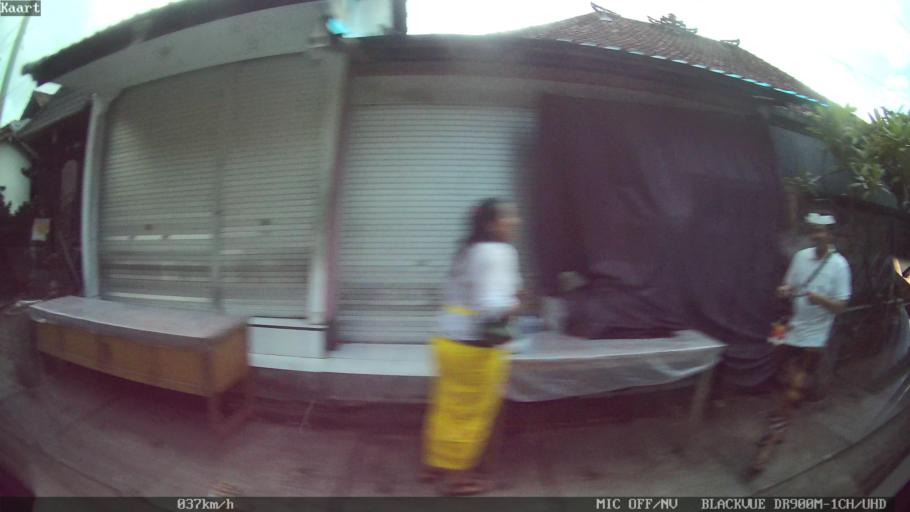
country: ID
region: Bali
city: Banjar Pasekan
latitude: -8.6037
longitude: 115.2931
